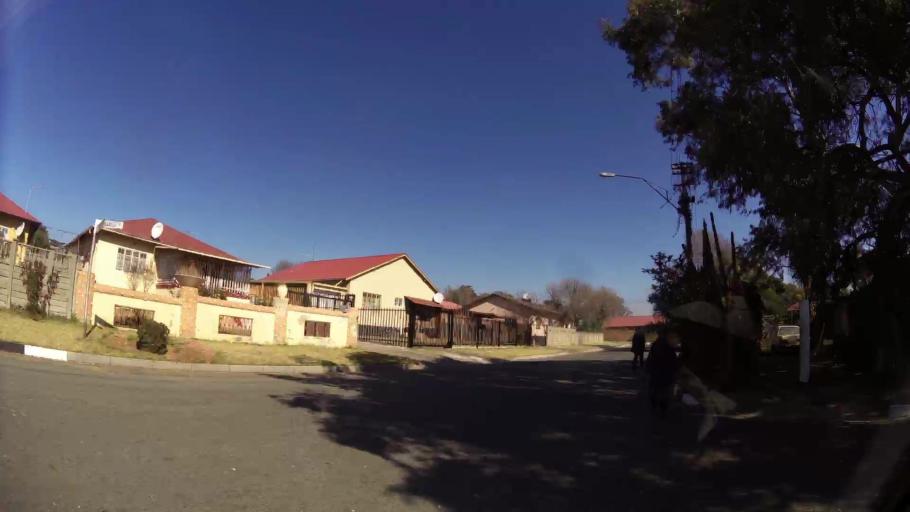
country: ZA
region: Gauteng
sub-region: City of Johannesburg Metropolitan Municipality
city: Johannesburg
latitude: -26.2403
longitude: 28.0916
